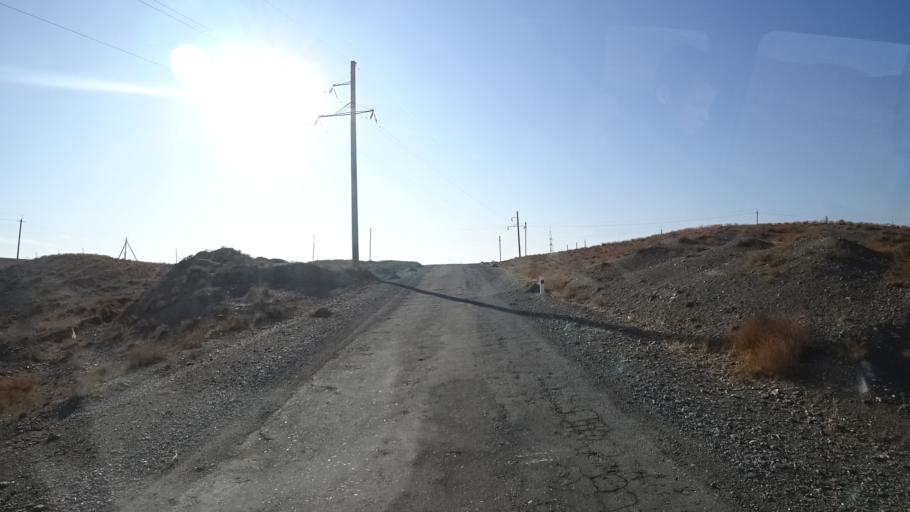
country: UZ
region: Navoiy
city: Beshrabot
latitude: 40.2333
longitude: 65.4186
